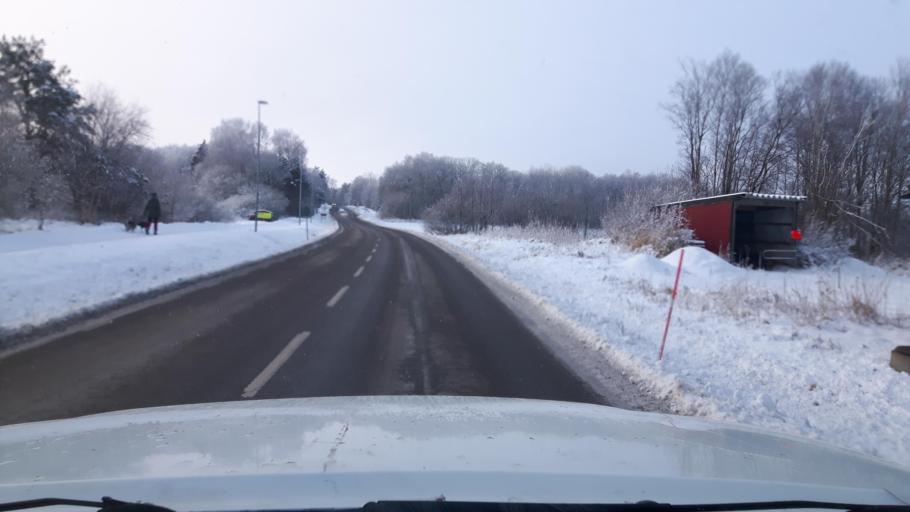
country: SE
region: Halland
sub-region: Kungsbacka Kommun
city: Vallda
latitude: 57.4502
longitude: 11.9552
